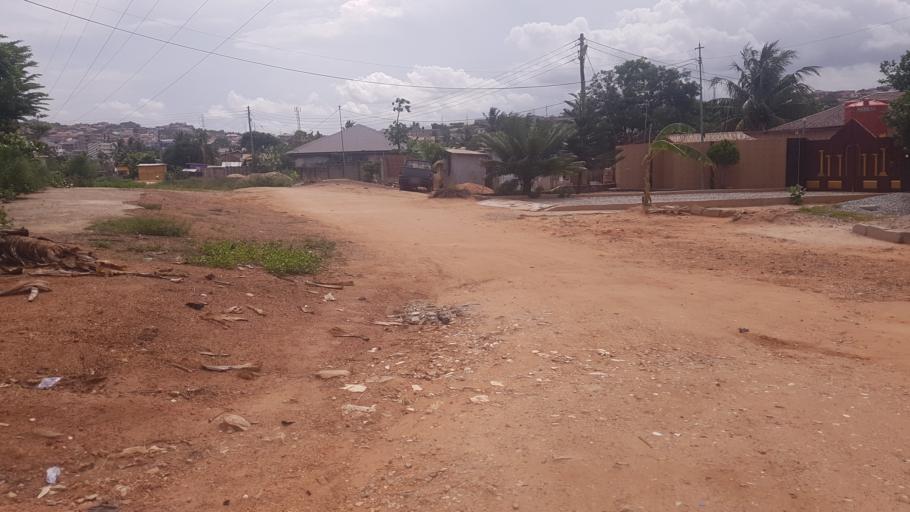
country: GH
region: Greater Accra
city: Gbawe
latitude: 5.5503
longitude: -0.3485
